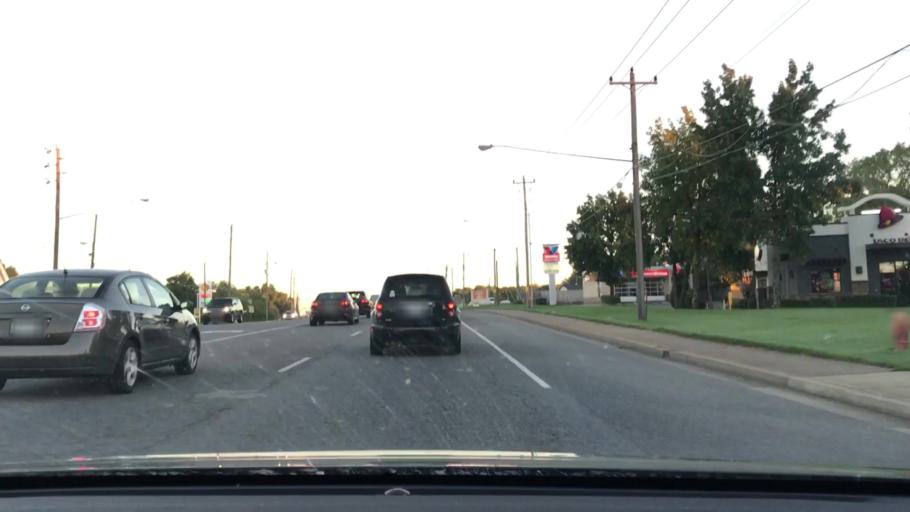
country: US
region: Tennessee
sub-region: Williamson County
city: Brentwood Estates
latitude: 36.0478
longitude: -86.7134
